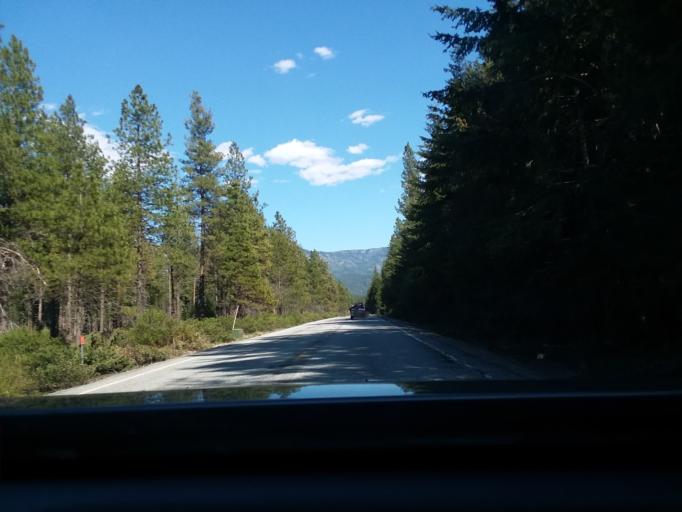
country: US
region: Washington
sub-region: Chelan County
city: Leavenworth
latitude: 47.8026
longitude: -120.6884
